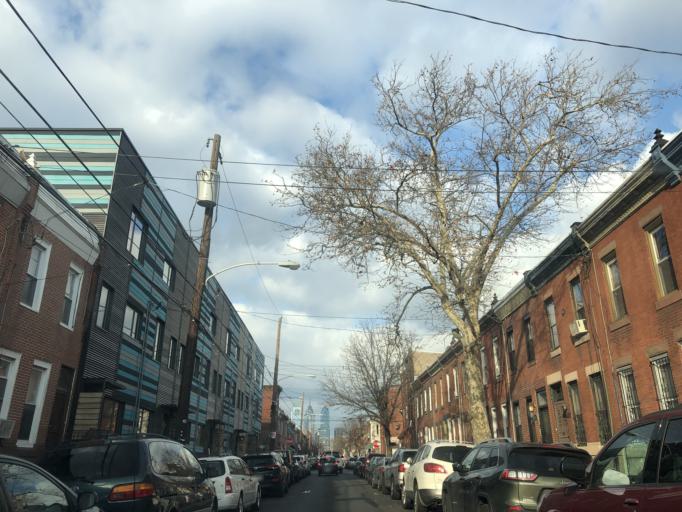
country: US
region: Pennsylvania
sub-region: Philadelphia County
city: Philadelphia
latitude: 39.9278
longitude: -75.1723
